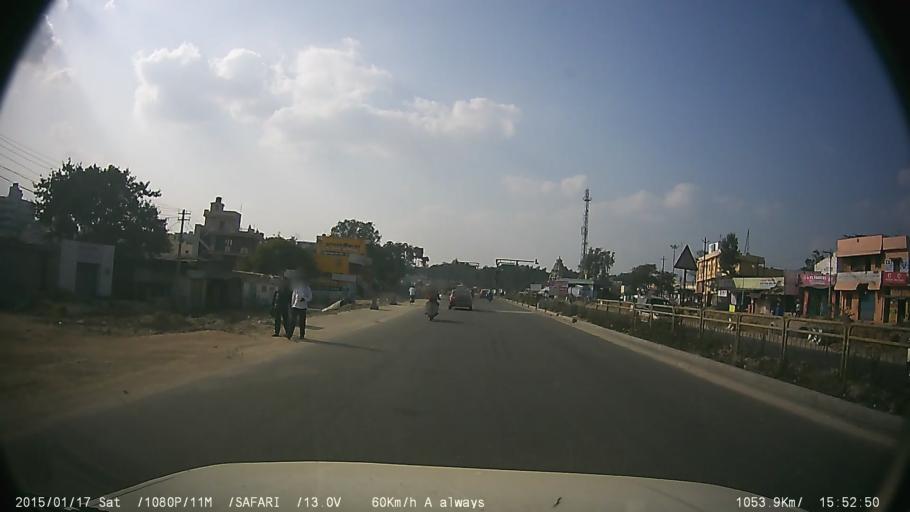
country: IN
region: Tamil Nadu
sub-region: Krishnagiri
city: Hosur
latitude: 12.7451
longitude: 77.8160
